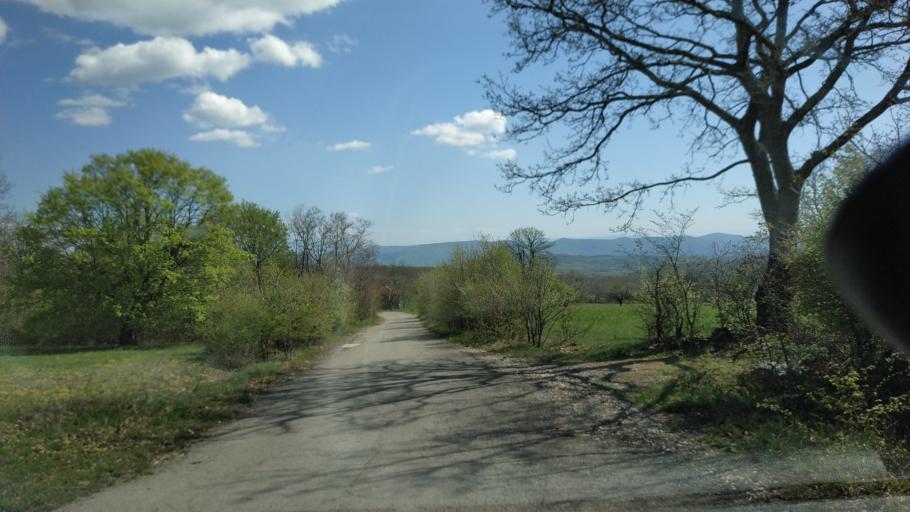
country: RS
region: Central Serbia
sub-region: Zajecarski Okrug
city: Soko Banja
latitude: 43.5514
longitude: 21.8972
